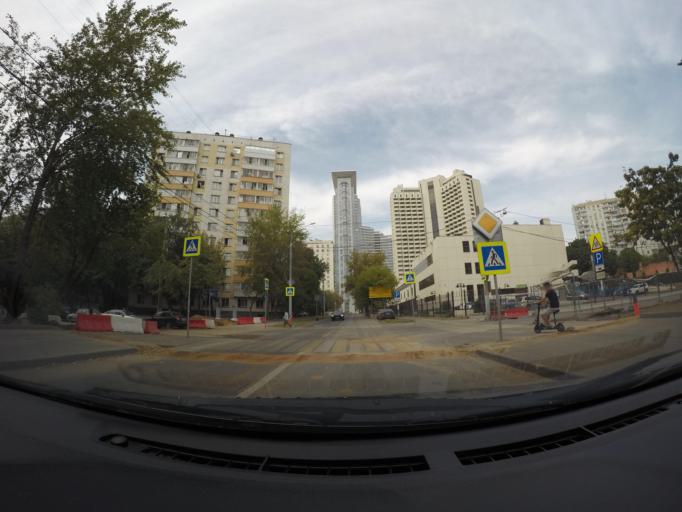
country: RU
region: Moscow
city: Sokol'niki
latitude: 55.7865
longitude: 37.6824
